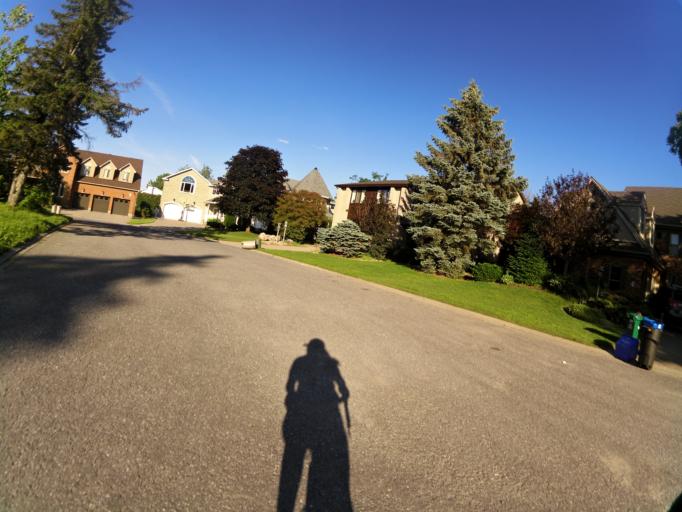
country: CA
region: Ontario
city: Bells Corners
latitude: 45.3321
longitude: -75.7644
